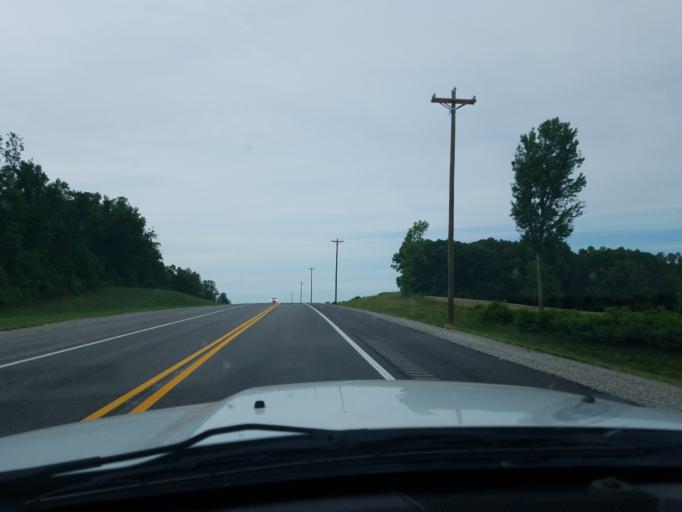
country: US
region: Tennessee
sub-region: Putnam County
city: Cookeville
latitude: 36.1622
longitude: -85.5633
